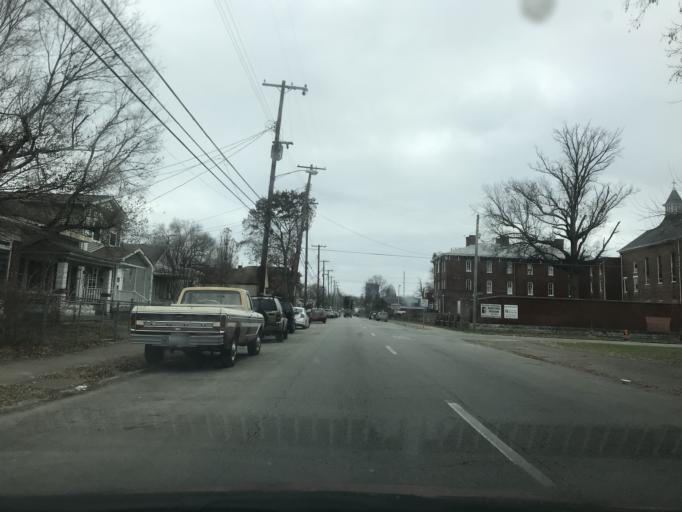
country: US
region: Kentucky
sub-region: Jefferson County
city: Louisville
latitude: 38.2679
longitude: -85.7871
